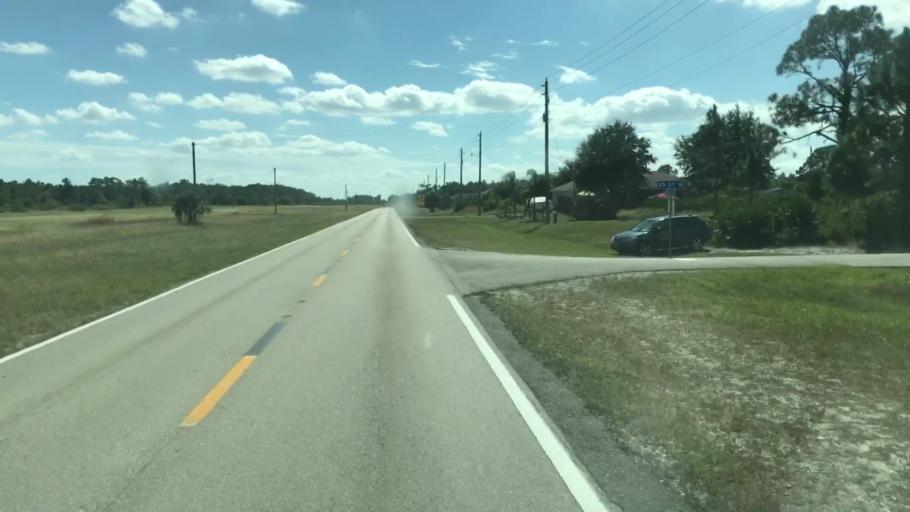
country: US
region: Florida
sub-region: Lee County
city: Lehigh Acres
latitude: 26.6556
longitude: -81.6637
